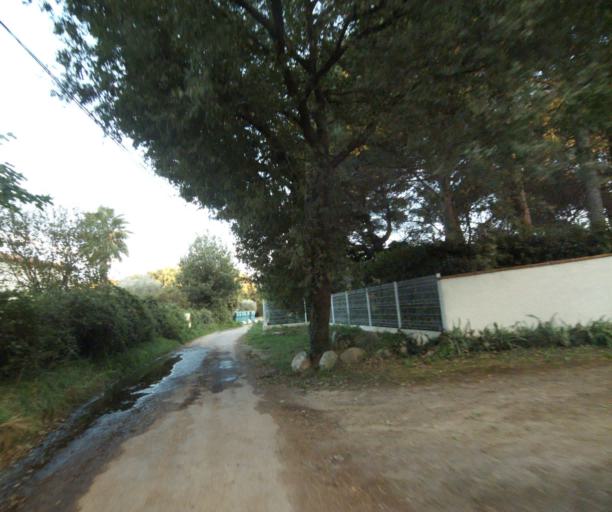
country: FR
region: Languedoc-Roussillon
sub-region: Departement des Pyrenees-Orientales
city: Argelers
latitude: 42.5731
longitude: 3.0139
